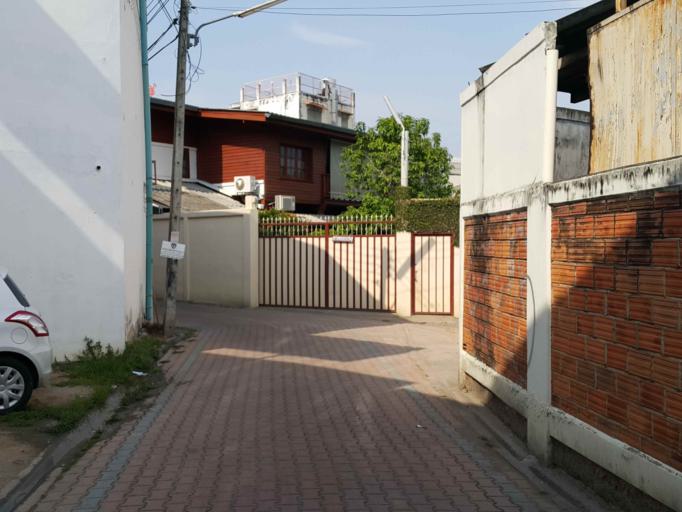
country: TH
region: Chiang Mai
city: Chiang Mai
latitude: 18.7872
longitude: 98.9920
